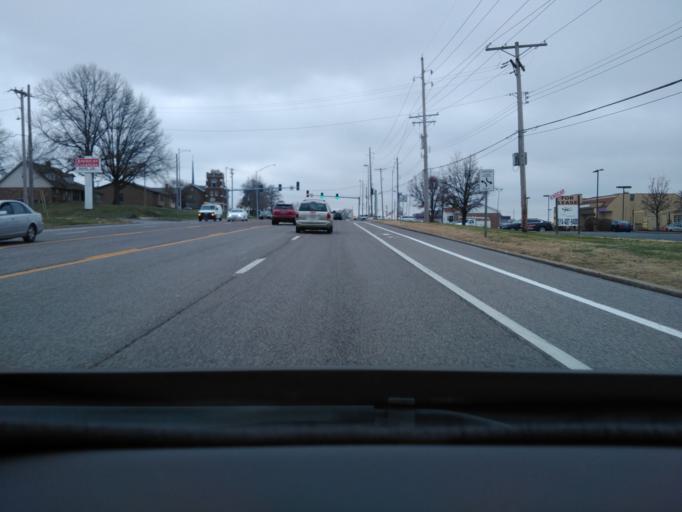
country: US
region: Missouri
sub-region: Saint Louis County
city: Oakville
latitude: 38.4742
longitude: -90.3045
